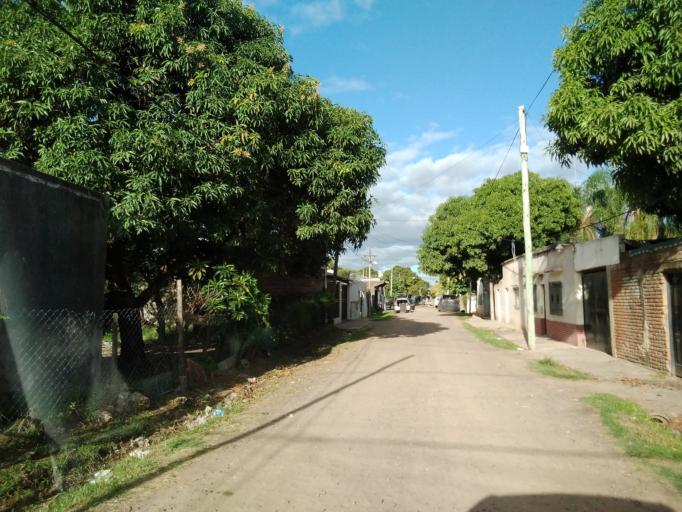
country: AR
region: Corrientes
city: Corrientes
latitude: -27.4778
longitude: -58.8120
